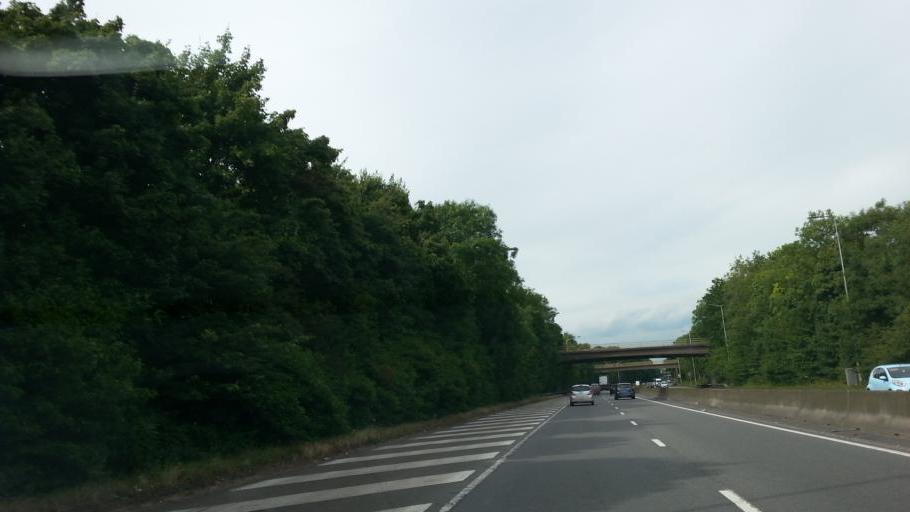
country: GB
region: Wales
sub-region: Cardiff
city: Cardiff
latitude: 51.5202
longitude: -3.1408
